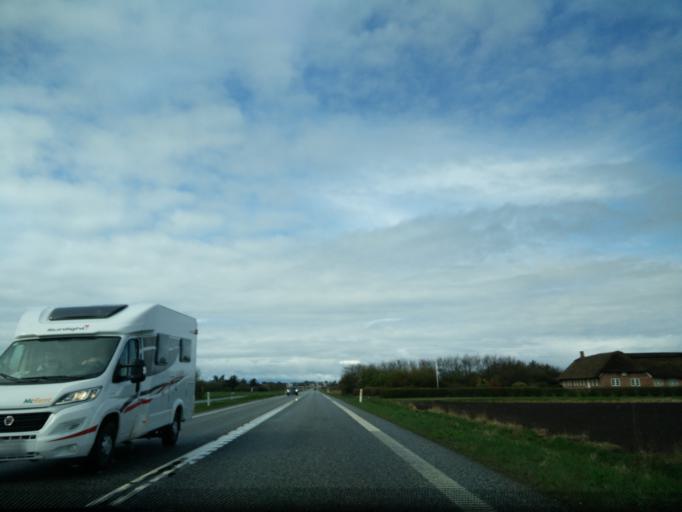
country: DK
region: Central Jutland
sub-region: Ringkobing-Skjern Kommune
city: Ringkobing
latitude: 56.1213
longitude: 8.1382
